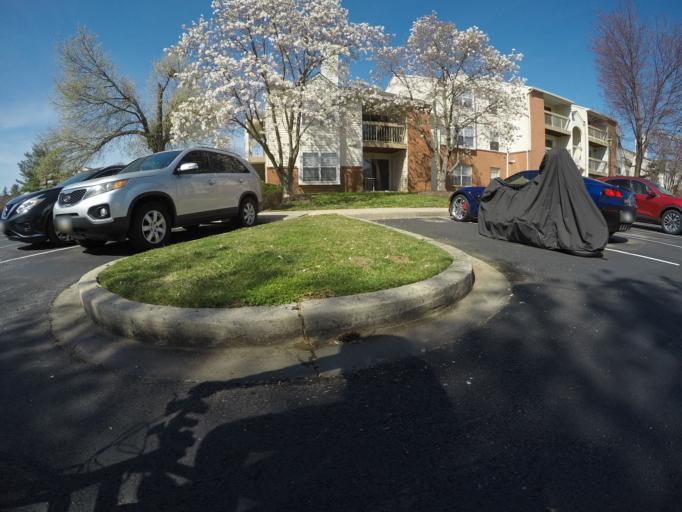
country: US
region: Maryland
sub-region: Frederick County
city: Ballenger Creek
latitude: 39.3773
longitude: -77.4268
